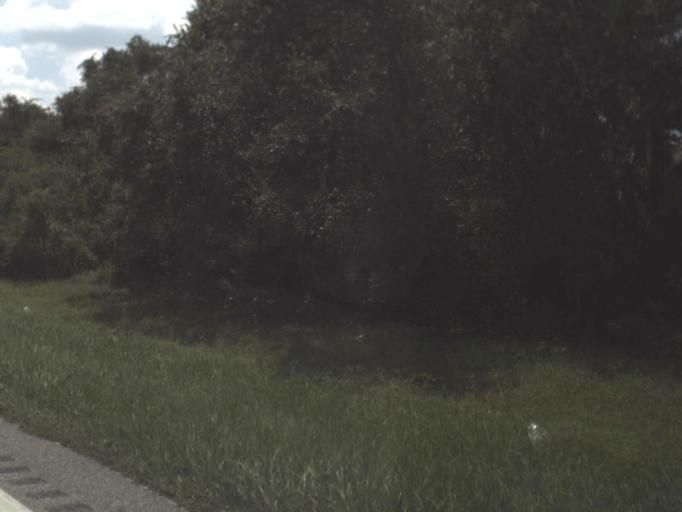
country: US
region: Florida
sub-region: Hillsborough County
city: Sun City Center
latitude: 27.6916
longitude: -82.3425
